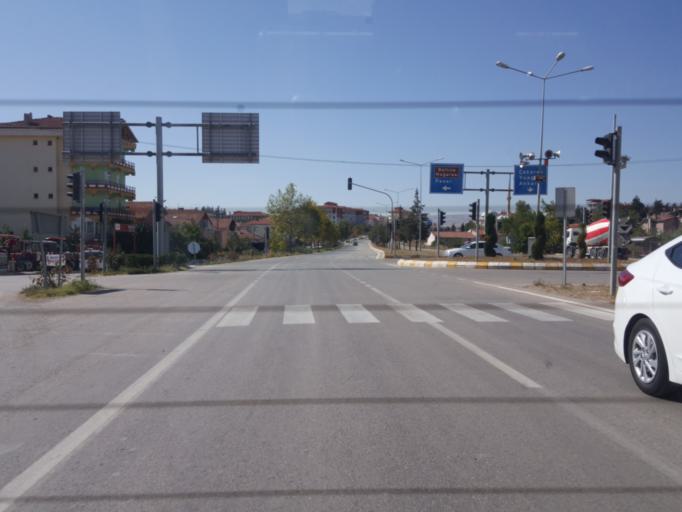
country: TR
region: Tokat
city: Zile
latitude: 40.2968
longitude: 35.8934
